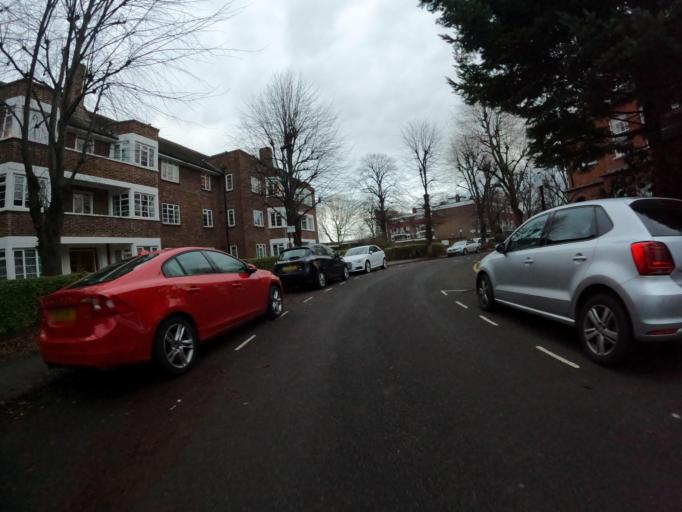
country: GB
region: England
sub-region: Greater London
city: Acton
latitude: 51.4917
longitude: -0.2739
